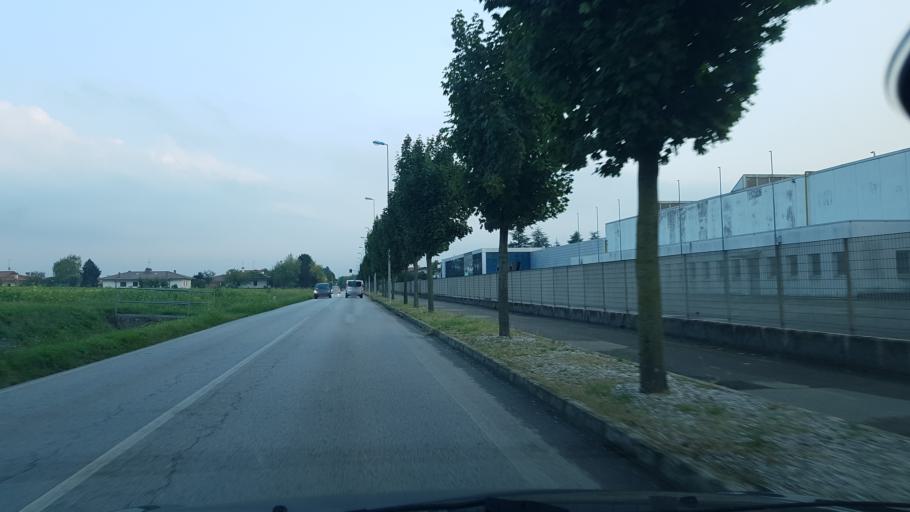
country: IT
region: Friuli Venezia Giulia
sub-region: Provincia di Udine
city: Trivignano Udinese
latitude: 45.9552
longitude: 13.3377
